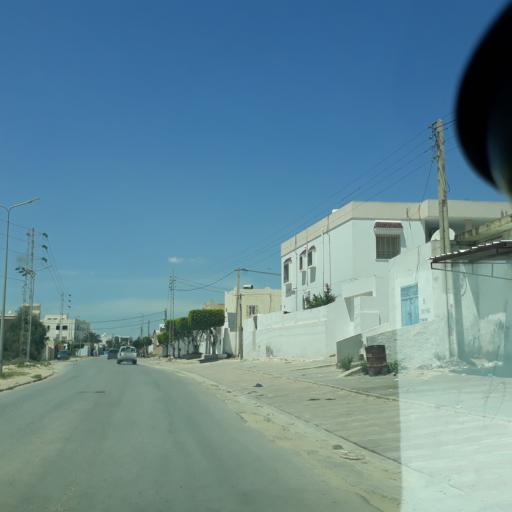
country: TN
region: Safaqis
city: Al Qarmadah
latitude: 34.8096
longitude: 10.7498
